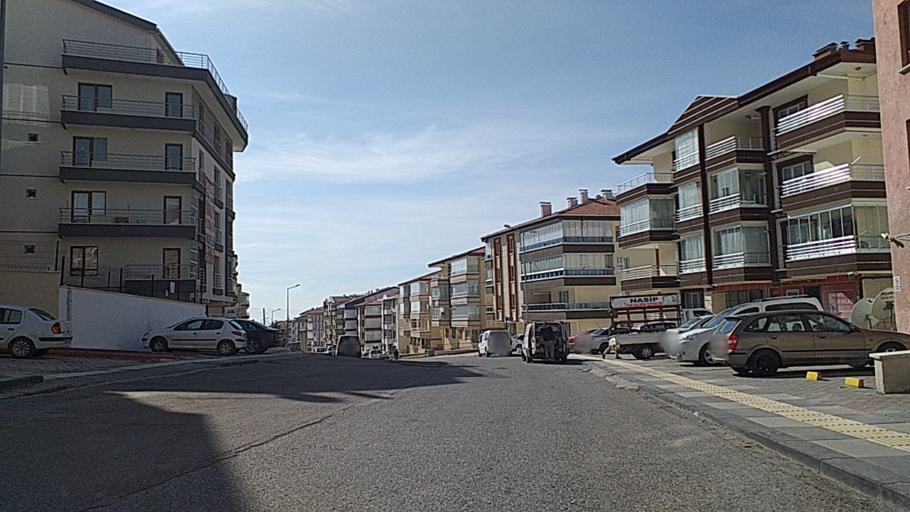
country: TR
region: Ankara
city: Ankara
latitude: 39.9924
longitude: 32.8116
